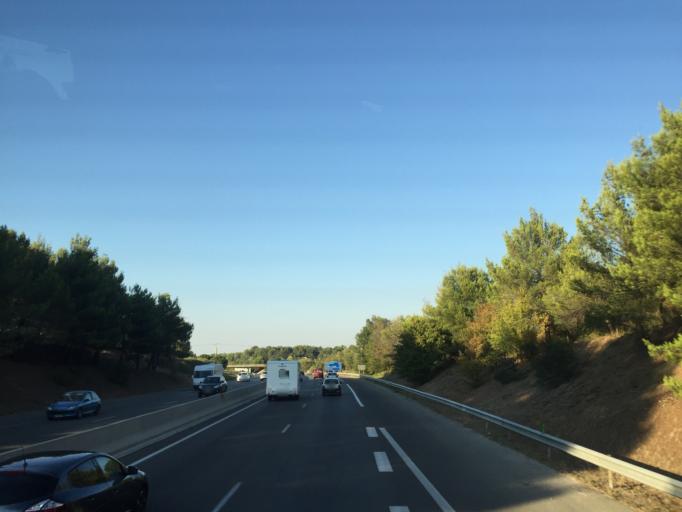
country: FR
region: Provence-Alpes-Cote d'Azur
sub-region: Departement des Bouches-du-Rhone
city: Venelles
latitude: 43.5753
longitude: 5.4717
